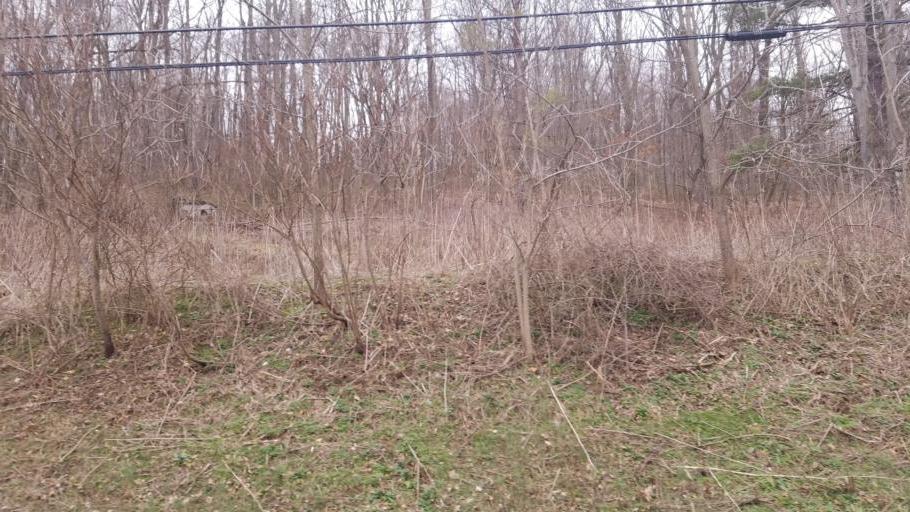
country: US
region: Ohio
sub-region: Sandusky County
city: Bellville
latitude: 40.6368
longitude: -82.5114
